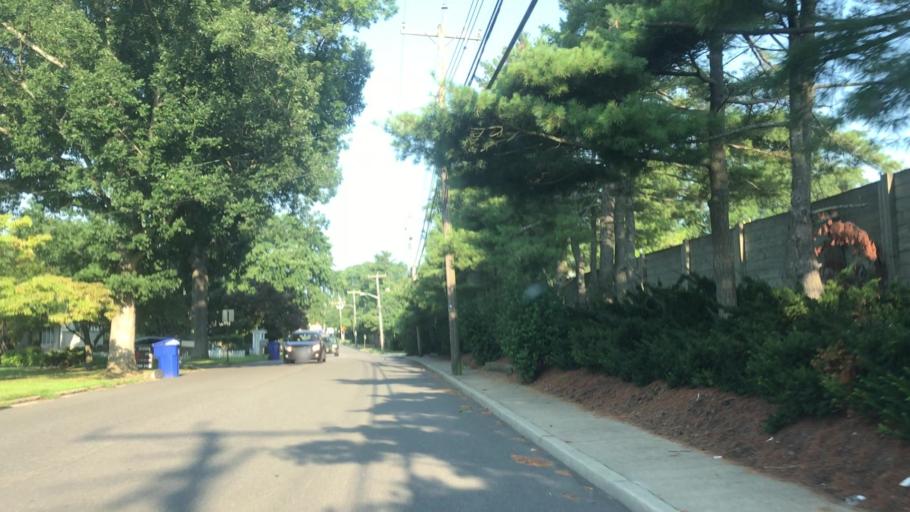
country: US
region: New Jersey
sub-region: Ocean County
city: Pine Beach
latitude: 39.9570
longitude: -74.1729
